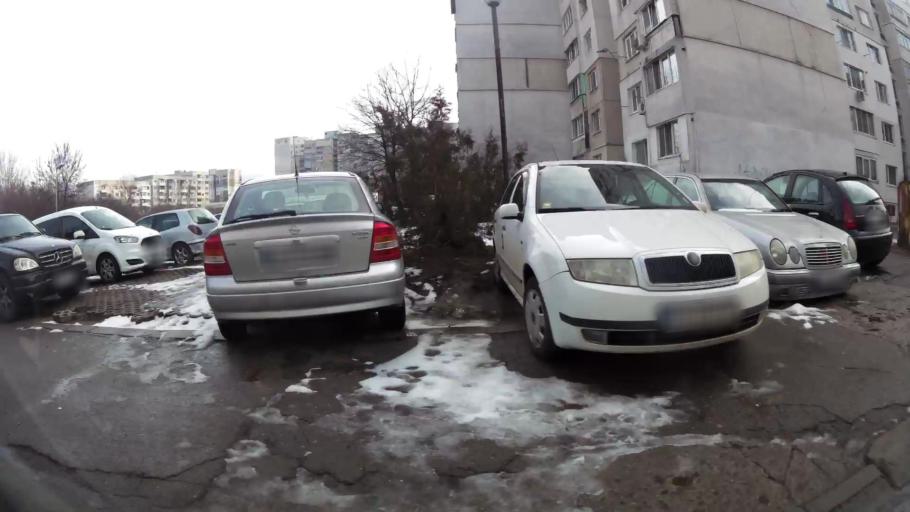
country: BG
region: Sofia-Capital
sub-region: Stolichna Obshtina
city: Sofia
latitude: 42.7153
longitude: 23.2714
